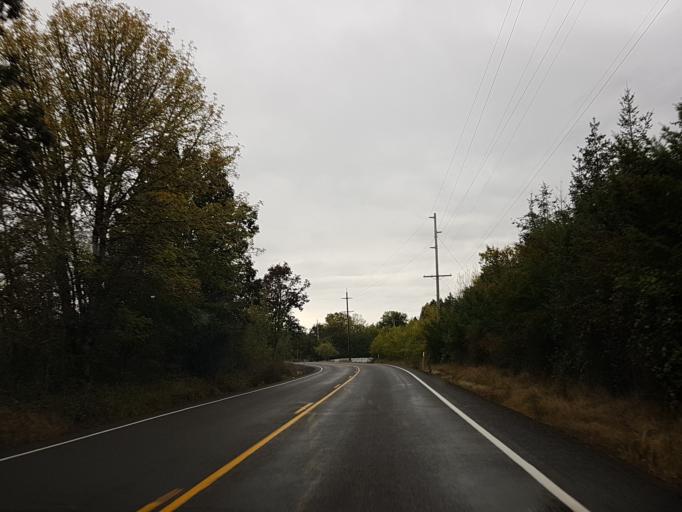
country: US
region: Oregon
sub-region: Marion County
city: Stayton
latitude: 44.7120
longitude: -122.7829
